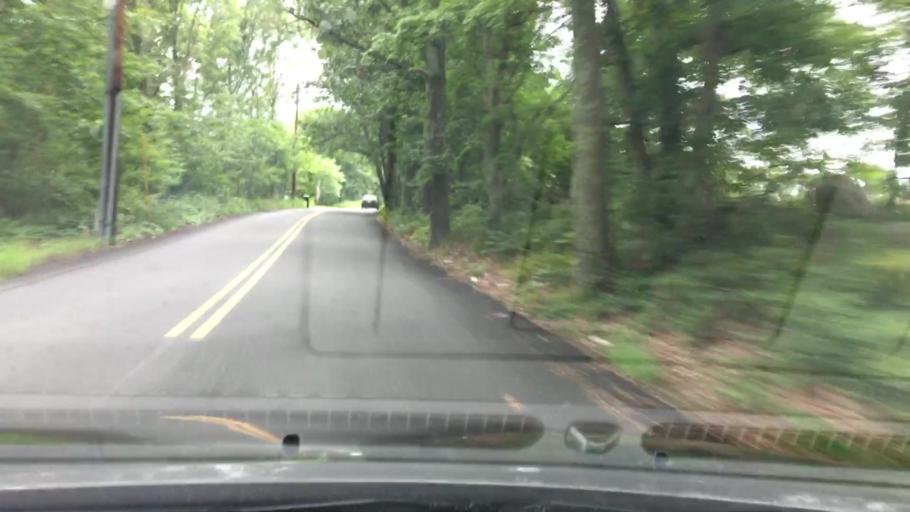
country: US
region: Rhode Island
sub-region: Providence County
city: Cumberland Hill
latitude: 42.0216
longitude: -71.4516
